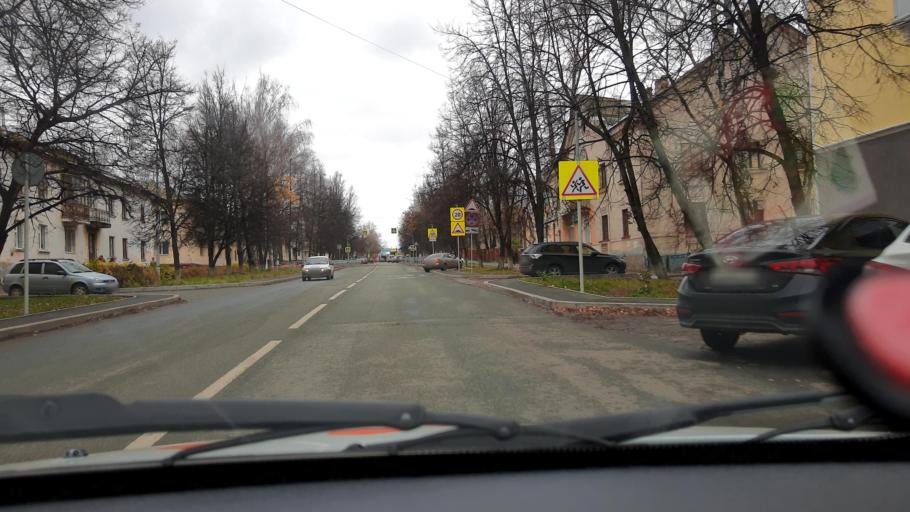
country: RU
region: Bashkortostan
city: Ufa
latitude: 54.8188
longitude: 56.0843
